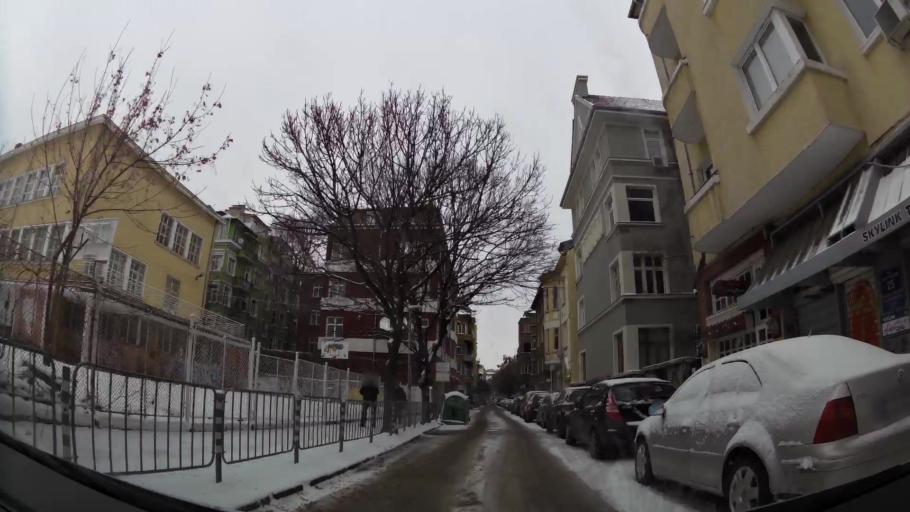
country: BG
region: Sofia-Capital
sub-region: Stolichna Obshtina
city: Sofia
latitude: 42.6907
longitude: 23.3220
